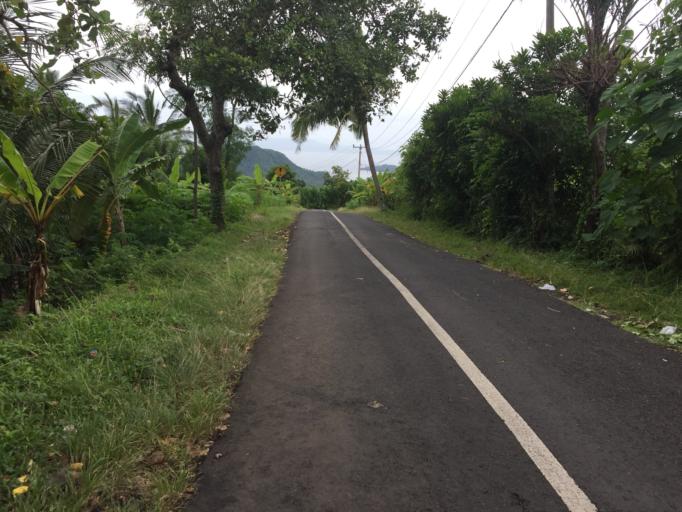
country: ID
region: Bali
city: Banjar Kawan
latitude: -8.4701
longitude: 115.5182
